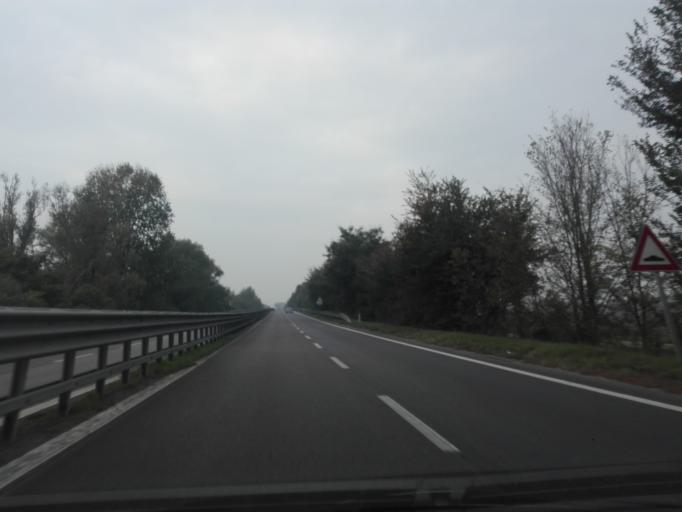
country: IT
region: Veneto
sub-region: Provincia di Rovigo
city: Fratta Polesine
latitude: 45.0212
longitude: 11.6558
